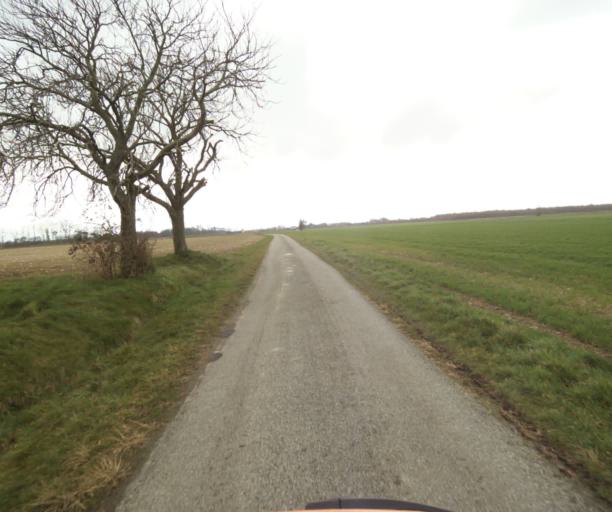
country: FR
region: Languedoc-Roussillon
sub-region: Departement de l'Aude
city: Belpech
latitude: 43.1777
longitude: 1.6930
